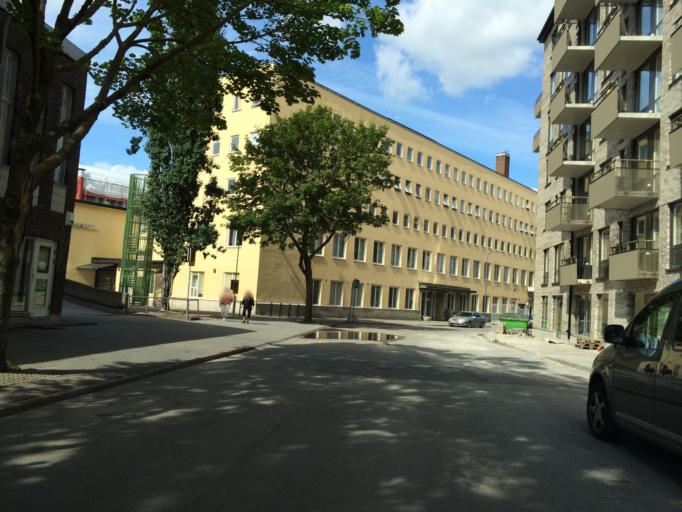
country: SE
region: Stockholm
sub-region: Stockholms Kommun
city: Arsta
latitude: 59.3129
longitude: 18.0251
